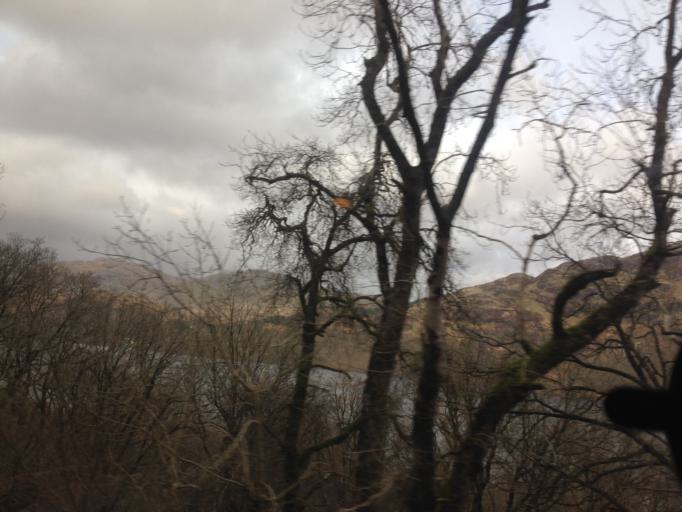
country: GB
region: Scotland
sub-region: Argyll and Bute
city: Garelochhead
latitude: 56.2256
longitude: -4.6994
